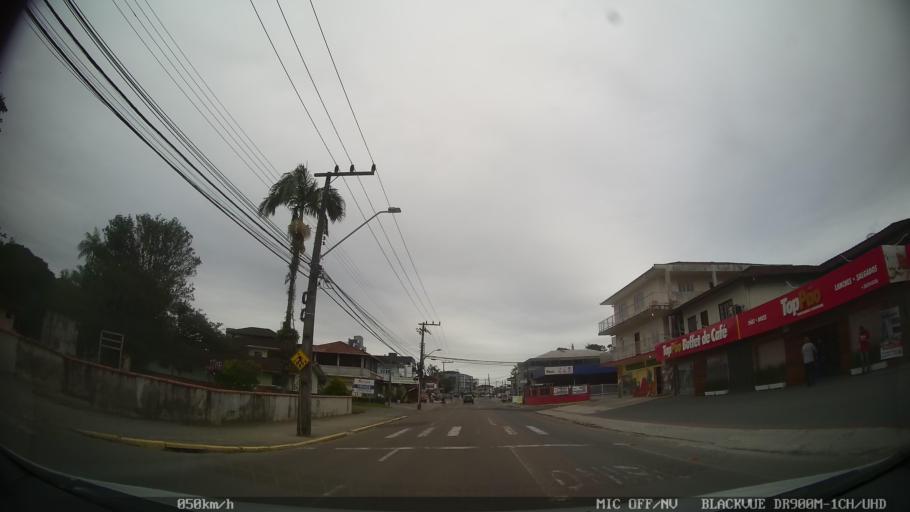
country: BR
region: Santa Catarina
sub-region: Joinville
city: Joinville
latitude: -26.2772
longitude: -48.8349
